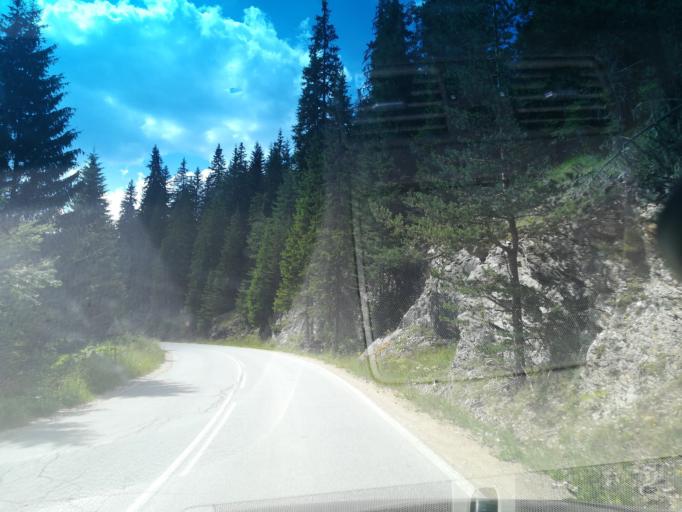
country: BG
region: Smolyan
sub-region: Obshtina Chepelare
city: Chepelare
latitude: 41.6616
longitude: 24.6695
